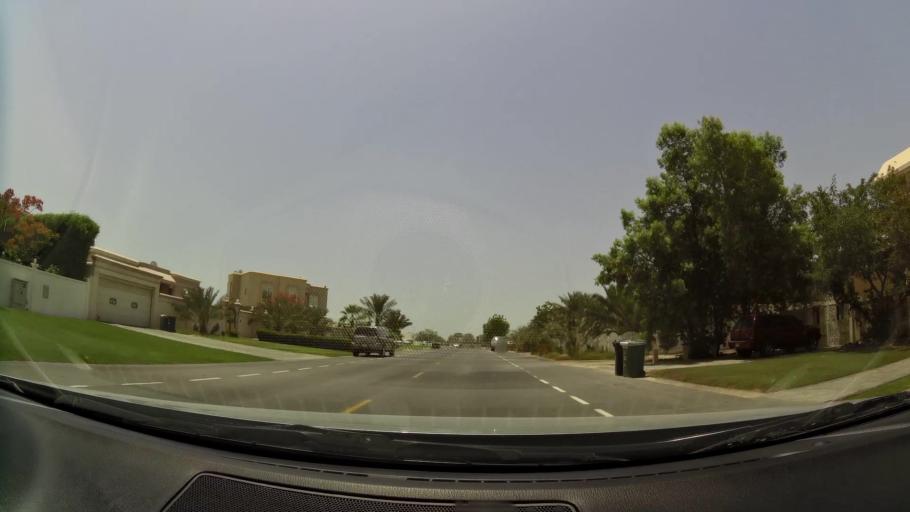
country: AE
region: Dubai
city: Dubai
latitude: 25.1649
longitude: 55.2193
